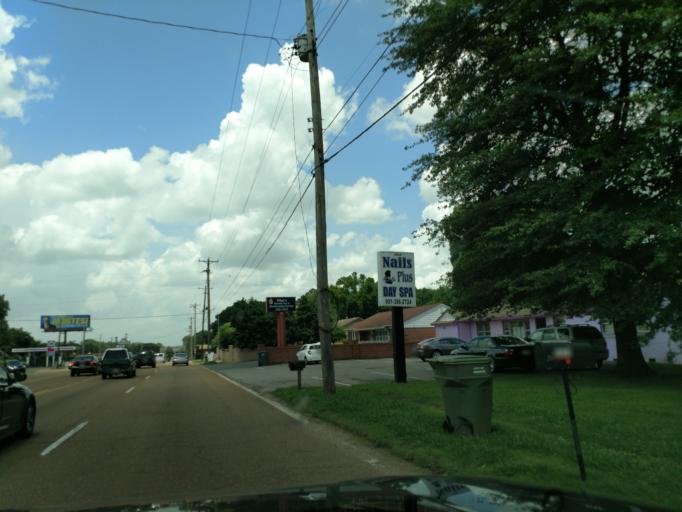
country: US
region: Mississippi
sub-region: De Soto County
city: Southaven
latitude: 35.0412
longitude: -90.0251
